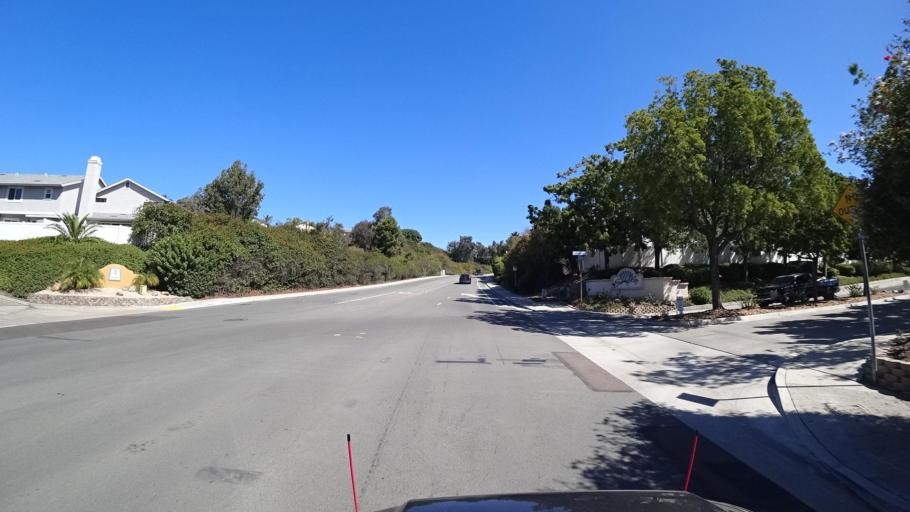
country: US
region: California
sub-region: San Diego County
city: Bonita
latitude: 32.6416
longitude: -117.0484
